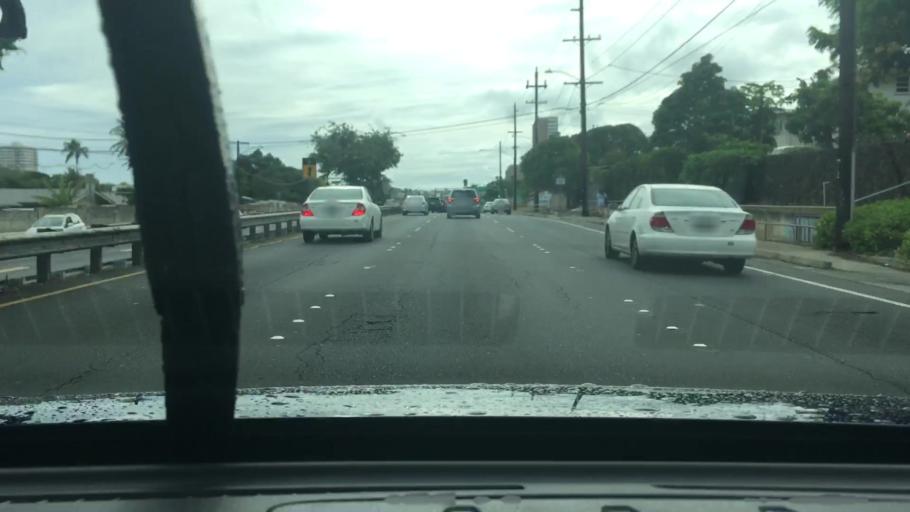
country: US
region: Hawaii
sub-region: Honolulu County
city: Honolulu
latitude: 21.2778
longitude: -157.7780
